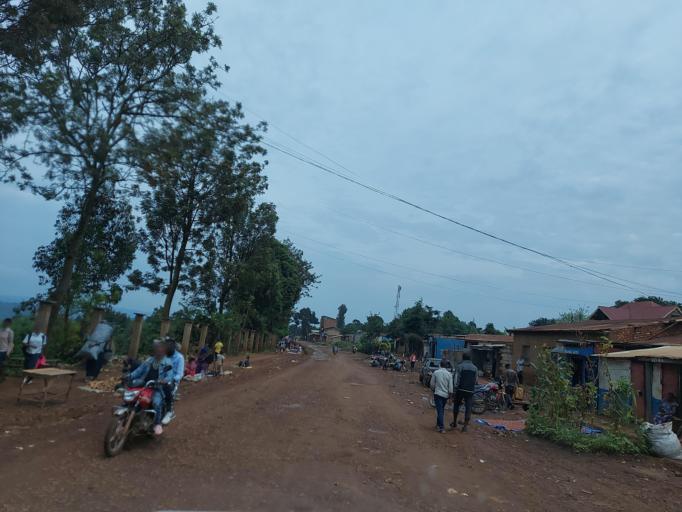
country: CD
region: South Kivu
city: Bukavu
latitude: -2.4827
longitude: 28.8197
